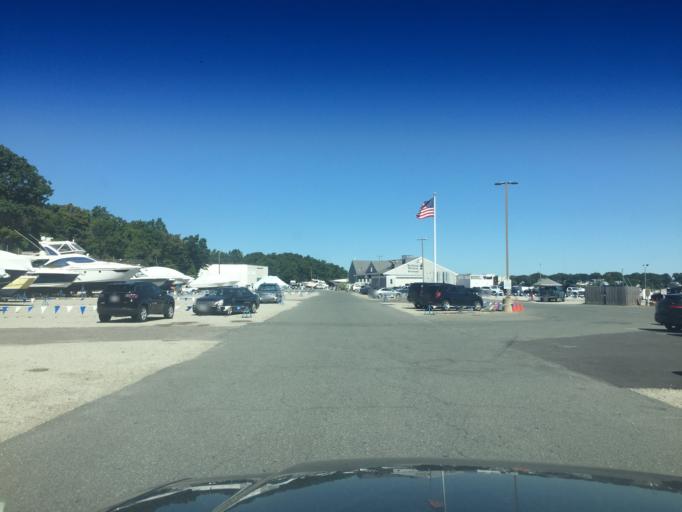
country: US
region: Massachusetts
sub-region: Norfolk County
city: Quincy
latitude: 42.2489
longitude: -70.9747
